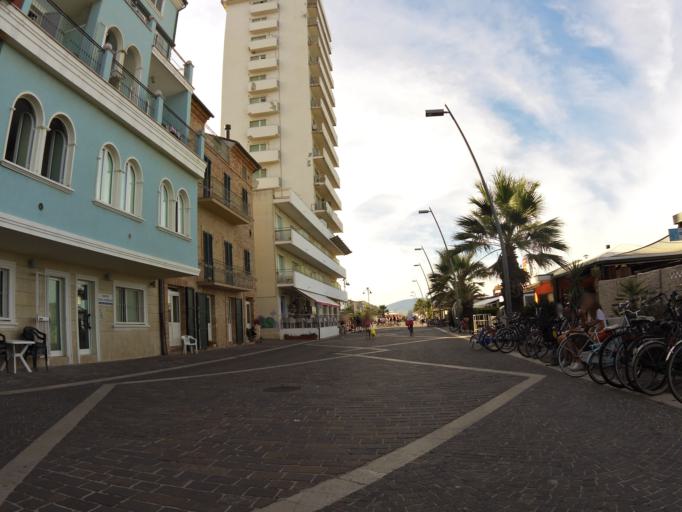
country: IT
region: The Marches
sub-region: Provincia di Macerata
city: Porto Recanati
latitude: 43.4349
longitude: 13.6644
